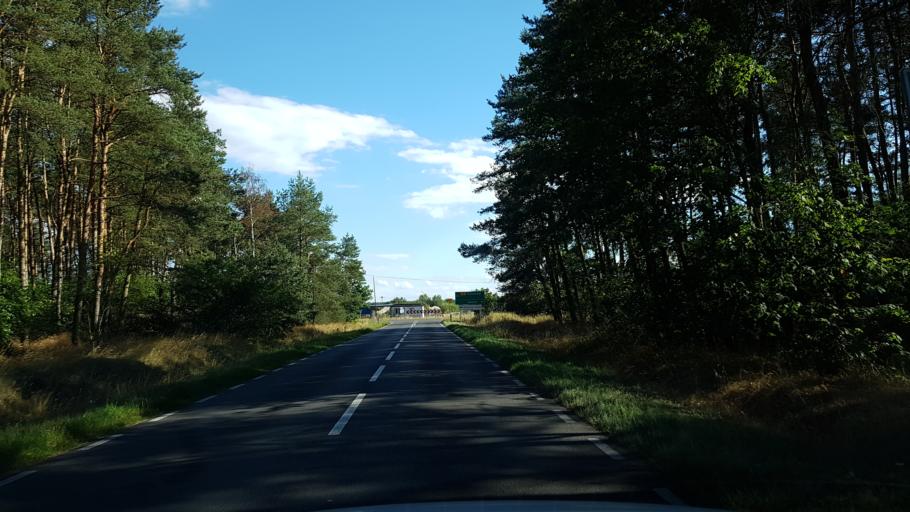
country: PL
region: West Pomeranian Voivodeship
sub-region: Powiat goleniowski
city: Goleniow
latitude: 53.5800
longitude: 14.7412
